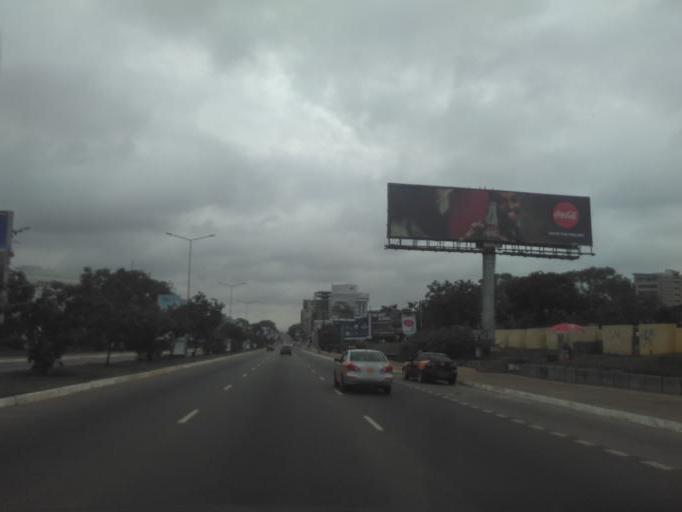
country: GH
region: Greater Accra
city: Accra
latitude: 5.5962
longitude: -0.1797
